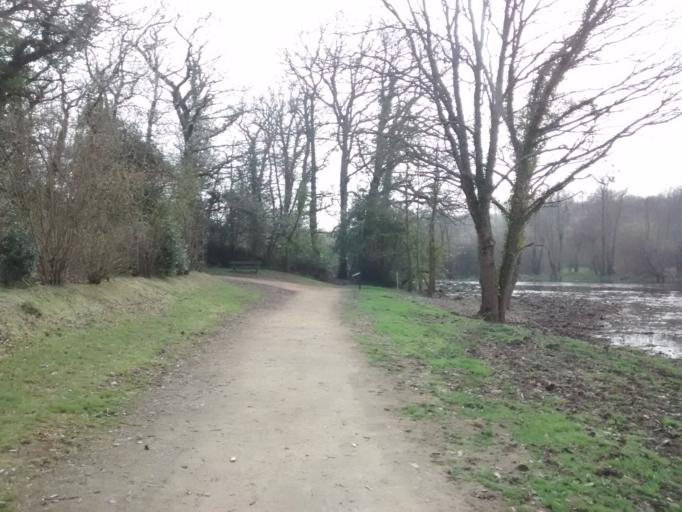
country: FR
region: Pays de la Loire
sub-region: Departement de la Loire-Atlantique
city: Carquefou
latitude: 47.2950
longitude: -1.5153
